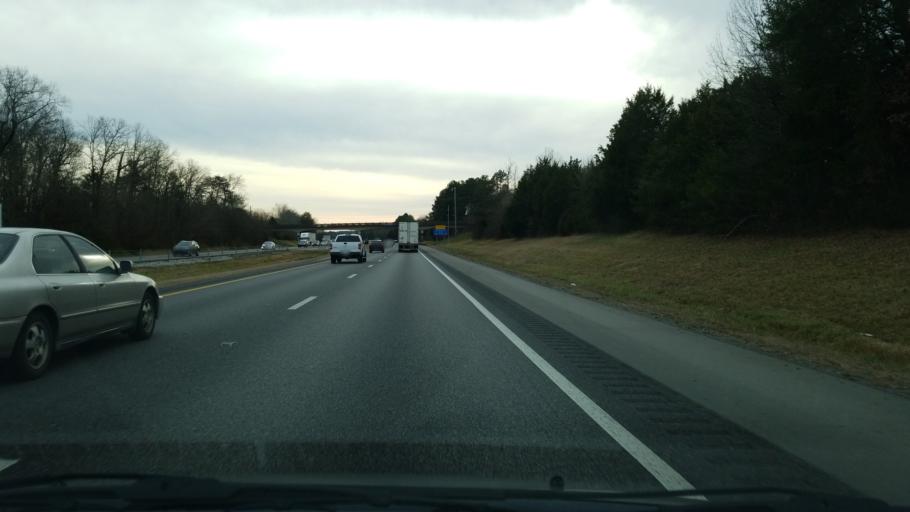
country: US
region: Tennessee
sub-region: Hamilton County
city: Collegedale
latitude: 35.1197
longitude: -85.0444
